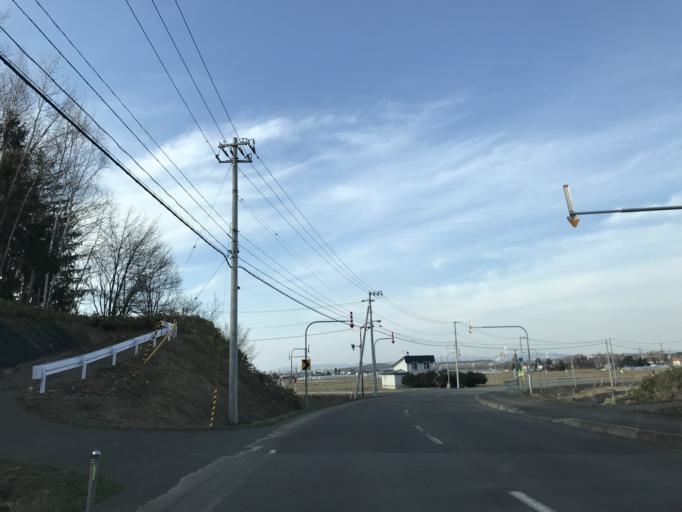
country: JP
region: Hokkaido
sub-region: Asahikawa-shi
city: Asahikawa
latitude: 43.7181
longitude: 142.3520
